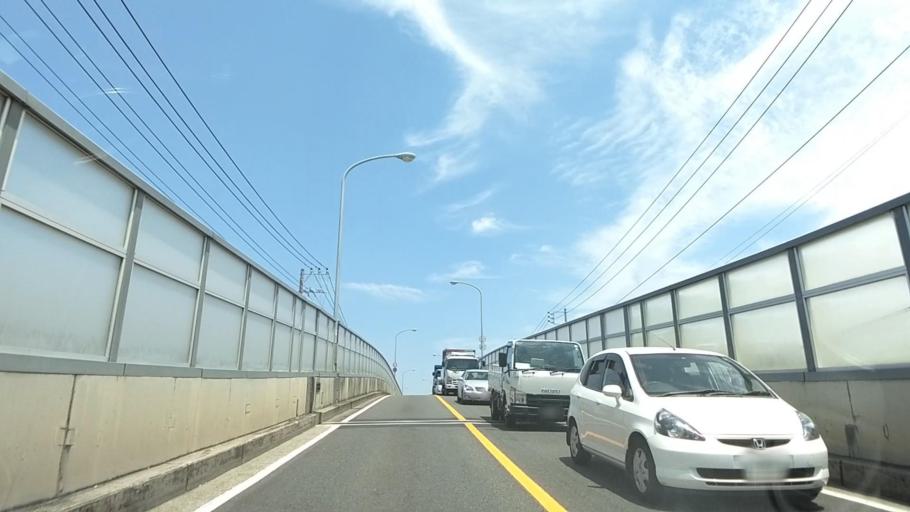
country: JP
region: Kanagawa
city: Minami-rinkan
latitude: 35.4687
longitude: 139.4804
